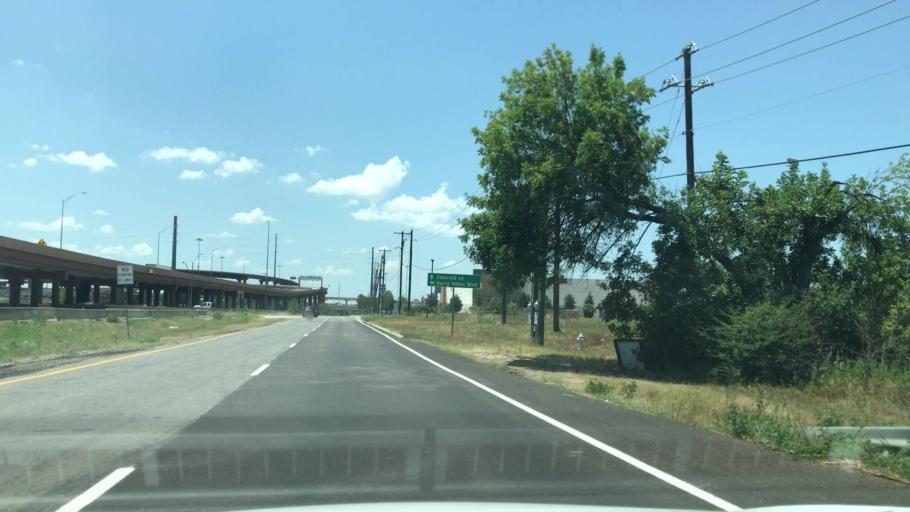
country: US
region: Texas
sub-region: Dallas County
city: Farmers Branch
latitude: 32.9156
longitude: -96.9001
